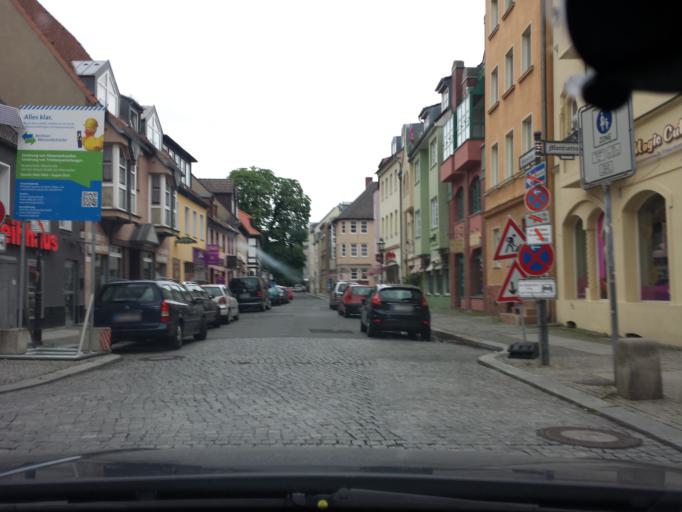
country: DE
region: Berlin
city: Spandau
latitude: 52.5379
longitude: 13.2026
